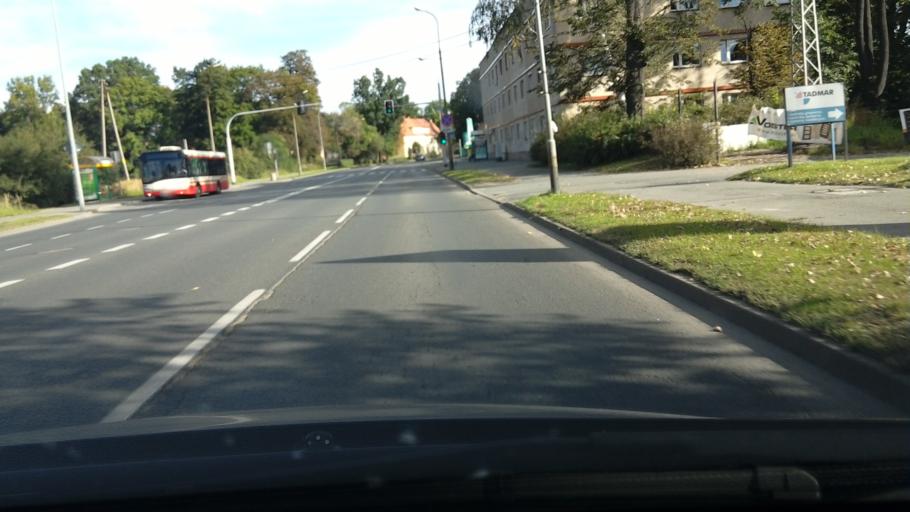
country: PL
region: Lower Silesian Voivodeship
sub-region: Jelenia Gora
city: Jelenia Gora
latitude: 50.8880
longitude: 15.7197
